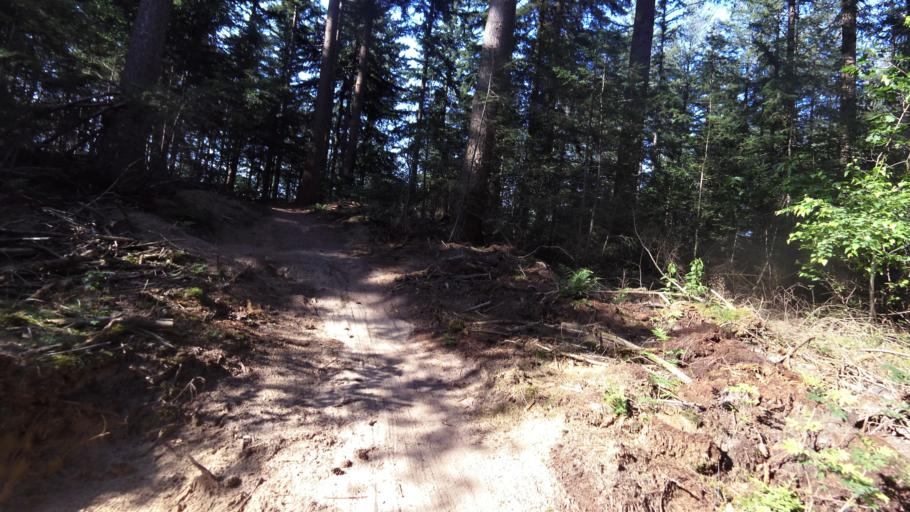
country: NL
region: Gelderland
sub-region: Gemeente Renkum
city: Oosterbeek
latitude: 52.0238
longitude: 5.8414
